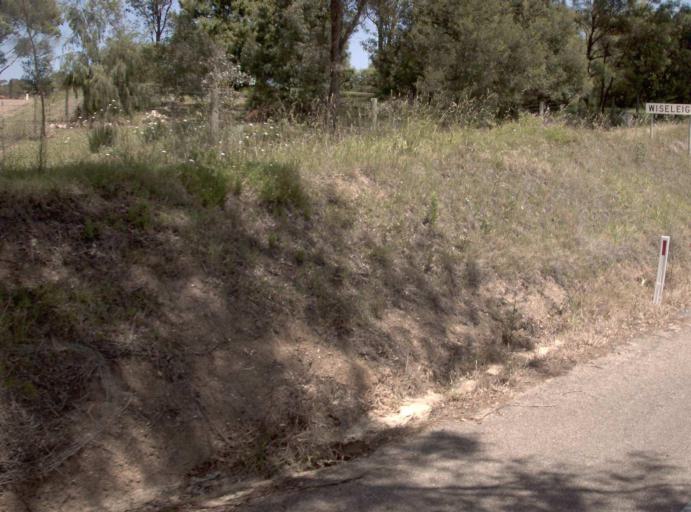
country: AU
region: Victoria
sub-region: East Gippsland
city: Bairnsdale
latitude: -37.7115
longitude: 147.8107
